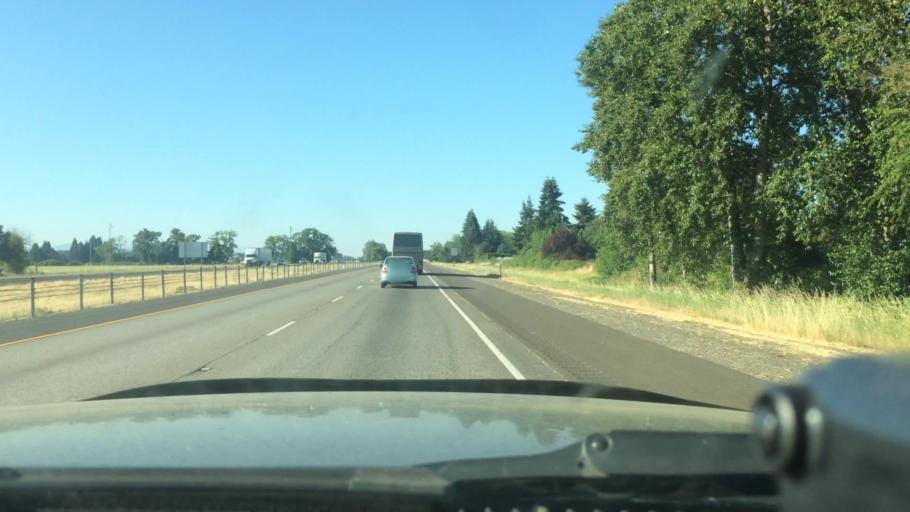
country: US
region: Oregon
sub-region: Linn County
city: Albany
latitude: 44.6100
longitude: -123.0623
